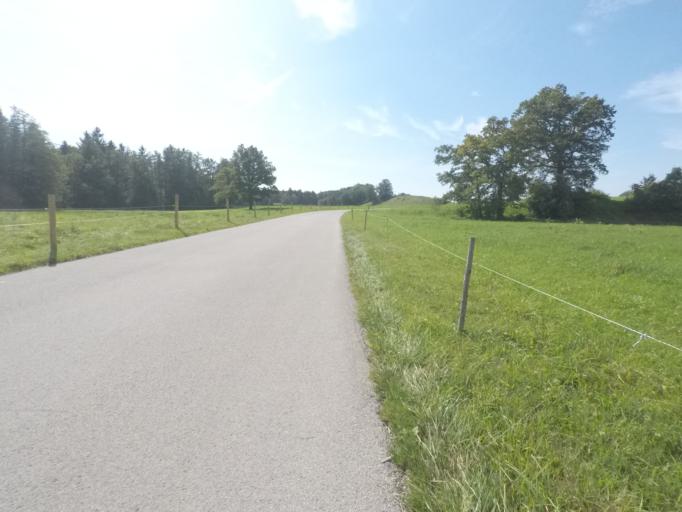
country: DE
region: Bavaria
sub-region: Upper Bavaria
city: Konigsdorf
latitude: 47.8257
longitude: 11.5127
